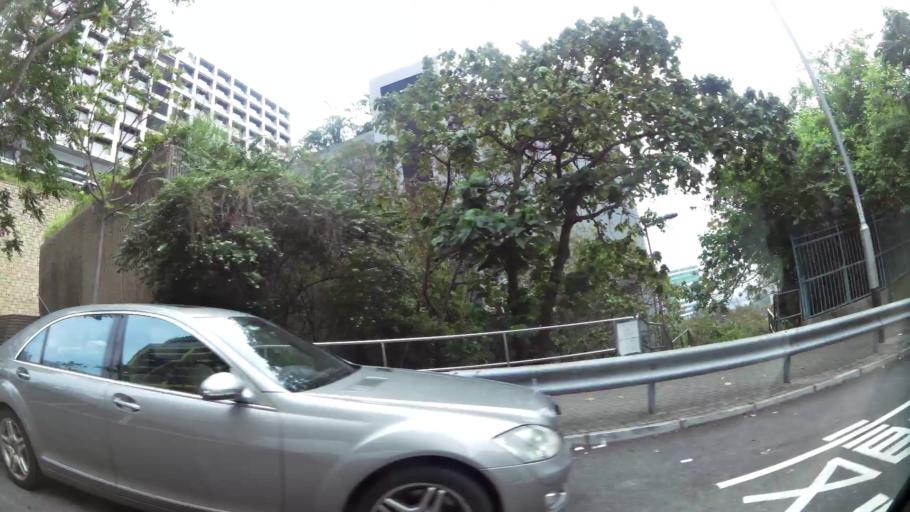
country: HK
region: Wanchai
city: Wan Chai
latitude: 22.2687
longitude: 114.2366
